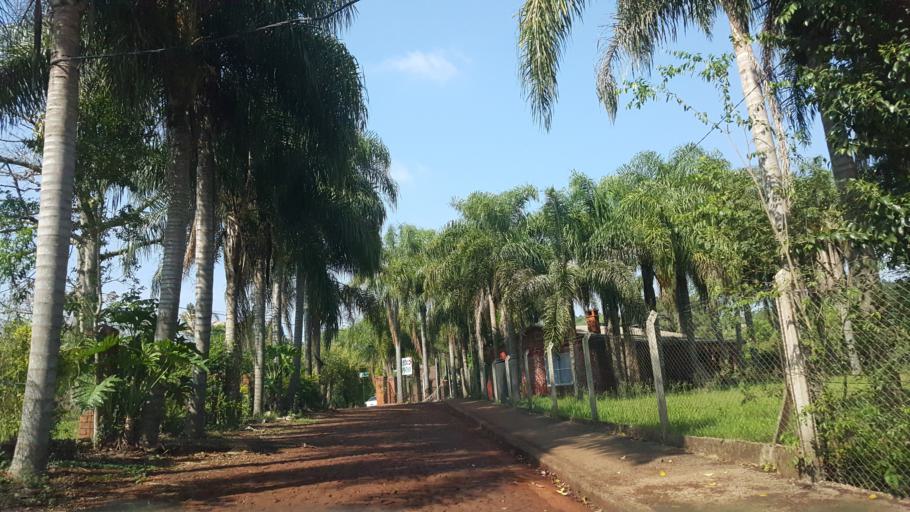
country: AR
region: Misiones
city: Capiovi
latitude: -26.9253
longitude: -55.0618
